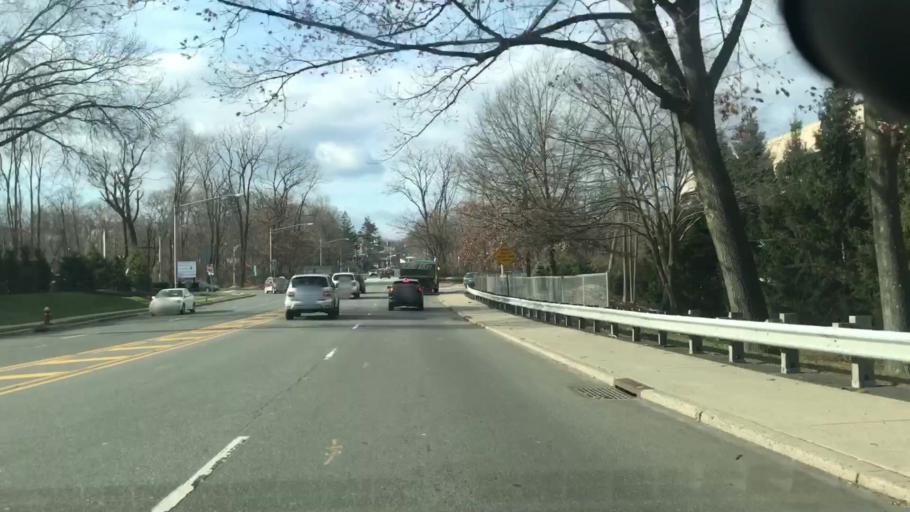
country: US
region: New Jersey
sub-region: Morris County
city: Morristown
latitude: 40.7887
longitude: -74.4668
